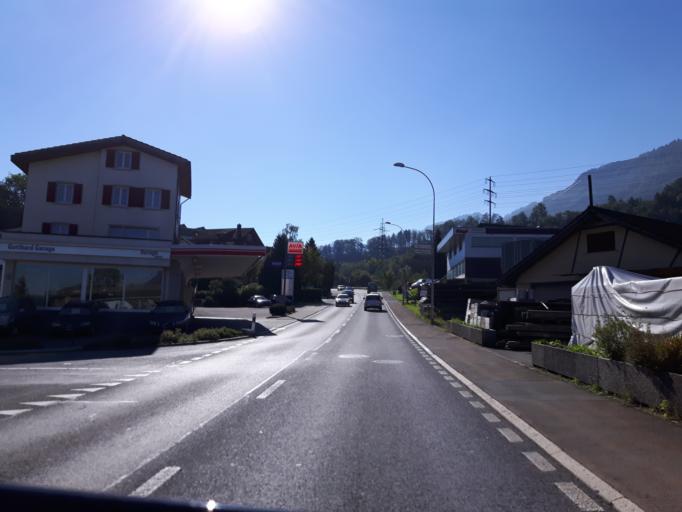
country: CH
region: Schwyz
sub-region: Bezirk Schwyz
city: Goldau
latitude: 47.0442
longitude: 8.5474
